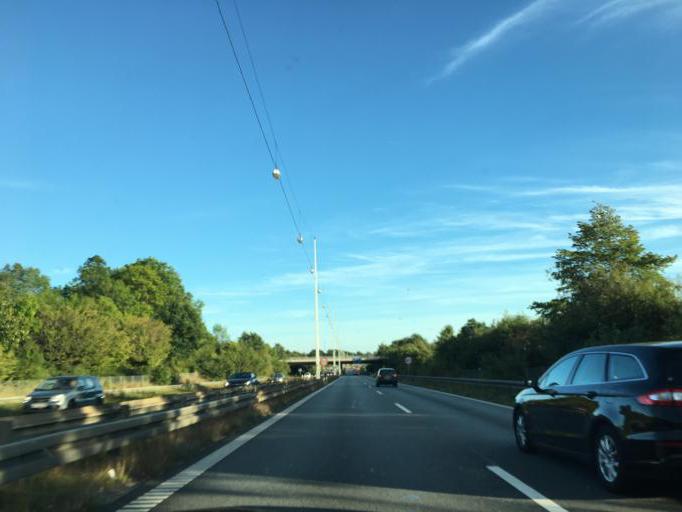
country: DK
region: Capital Region
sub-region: Kobenhavn
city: Vanlose
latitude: 55.7204
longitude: 12.4945
